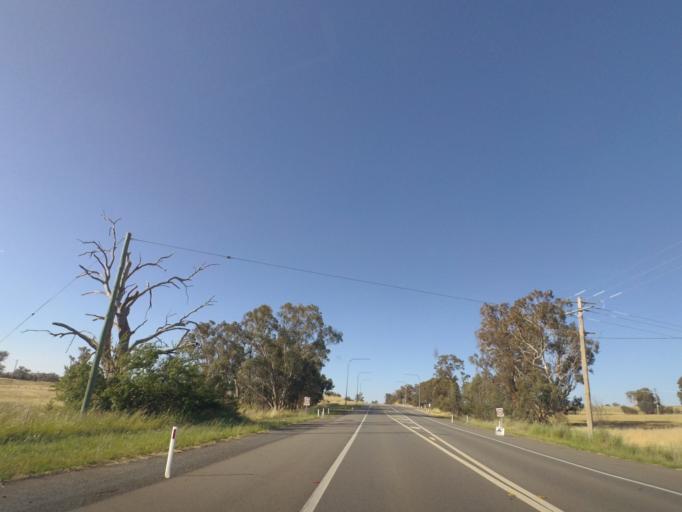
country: AU
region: New South Wales
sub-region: Wagga Wagga
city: Forest Hill
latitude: -35.2688
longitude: 147.7453
